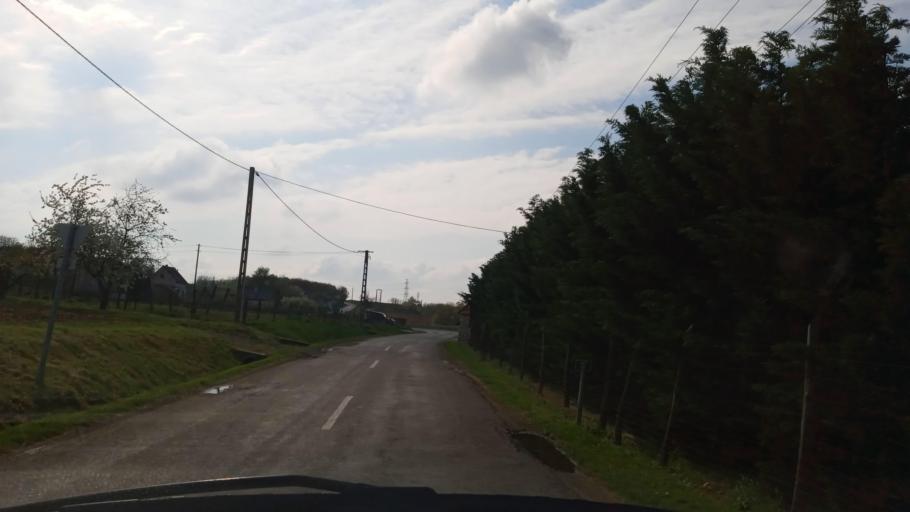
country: HU
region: Baranya
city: Pecsvarad
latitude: 46.1585
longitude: 18.4337
